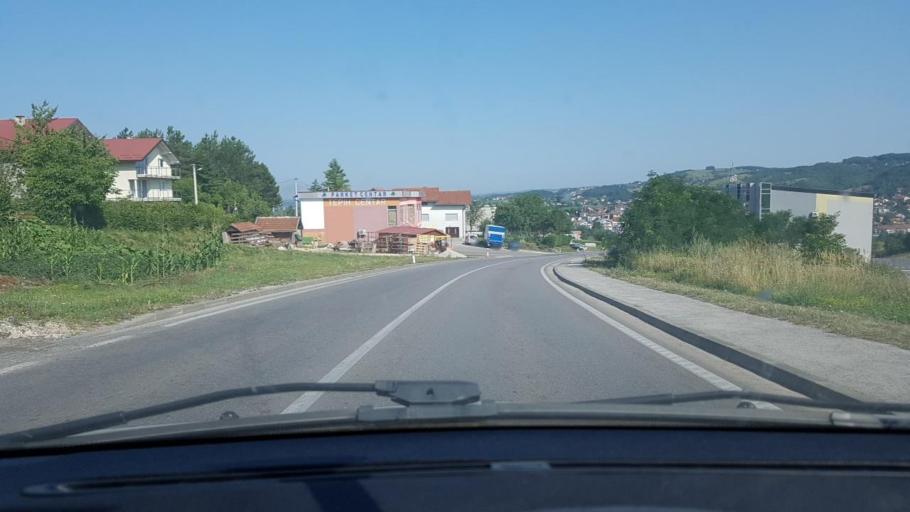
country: BA
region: Federation of Bosnia and Herzegovina
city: Cazin
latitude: 44.9547
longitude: 15.9398
